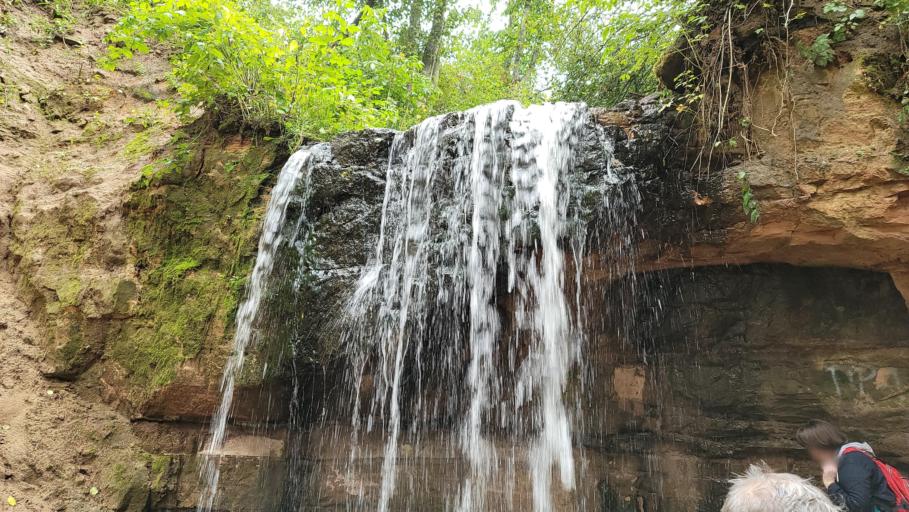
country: RU
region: Leningrad
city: Staraya Ladoga
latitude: 60.0192
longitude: 32.3310
